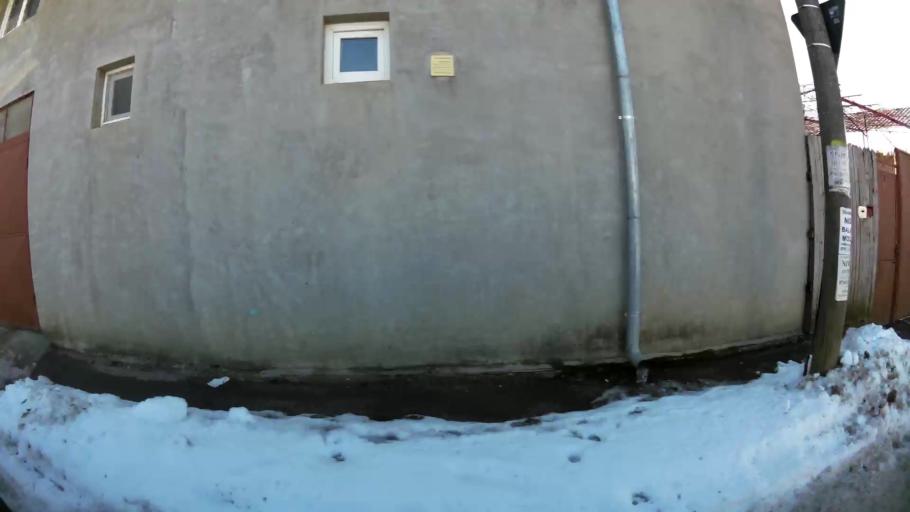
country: RO
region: Ilfov
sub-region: Comuna Magurele
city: Magurele
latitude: 44.3828
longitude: 26.0517
